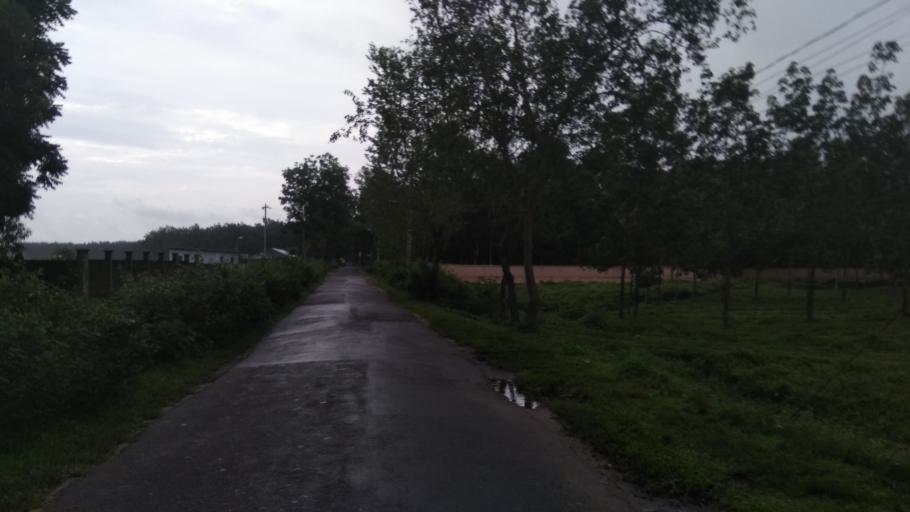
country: IN
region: Tripura
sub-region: Dhalai
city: Kamalpur
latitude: 24.3000
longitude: 91.7361
